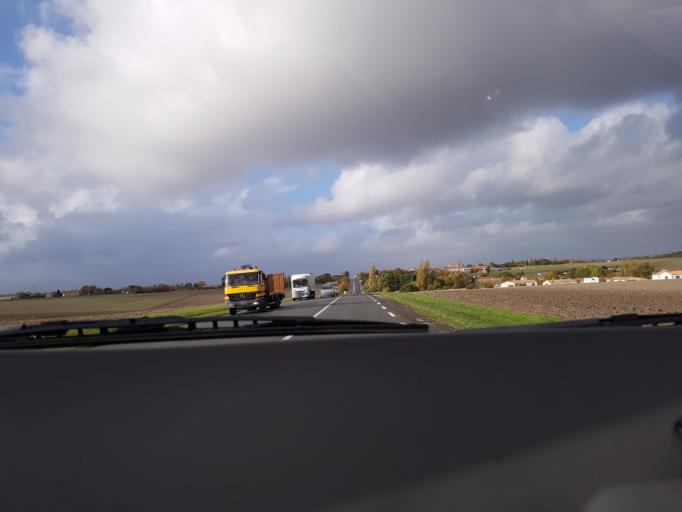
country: FR
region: Poitou-Charentes
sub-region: Departement de la Charente-Maritime
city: Thenac
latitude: 45.6467
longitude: -0.5835
